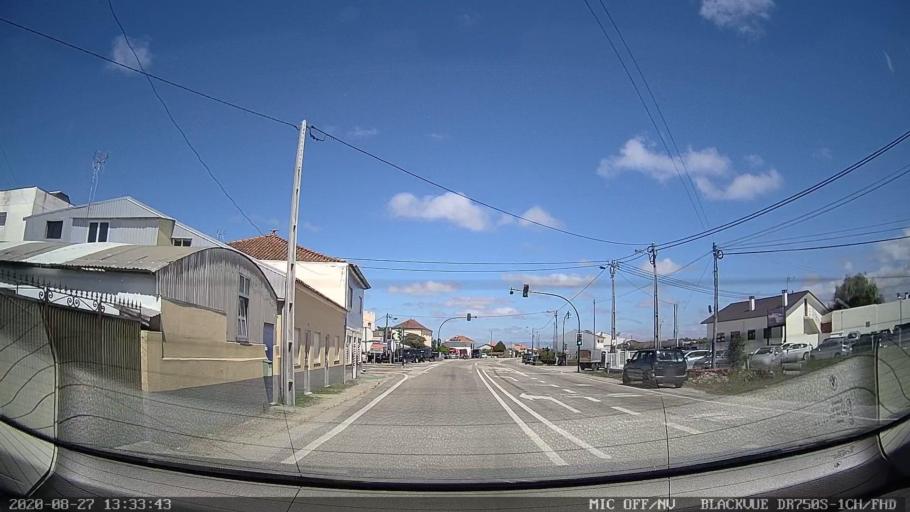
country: PT
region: Coimbra
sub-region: Mira
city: Mira
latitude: 40.4766
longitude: -8.6955
